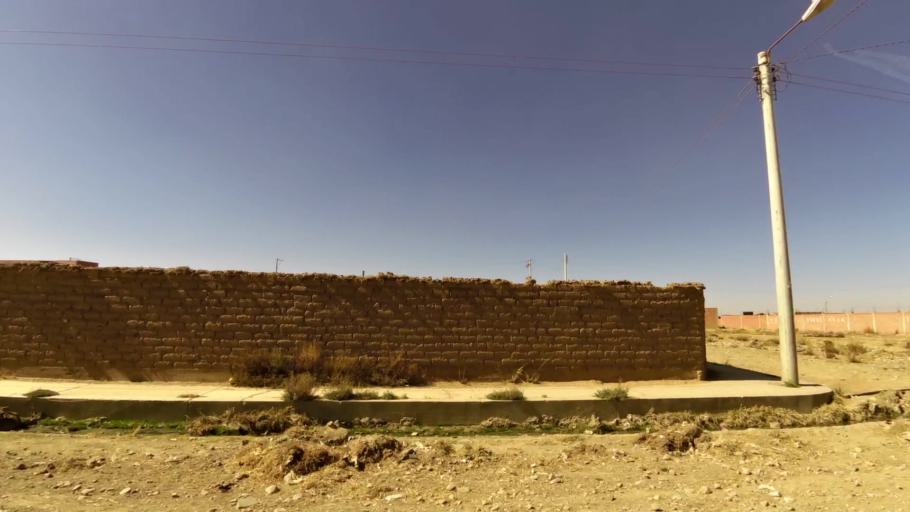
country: BO
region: La Paz
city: La Paz
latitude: -16.5853
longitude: -68.2091
